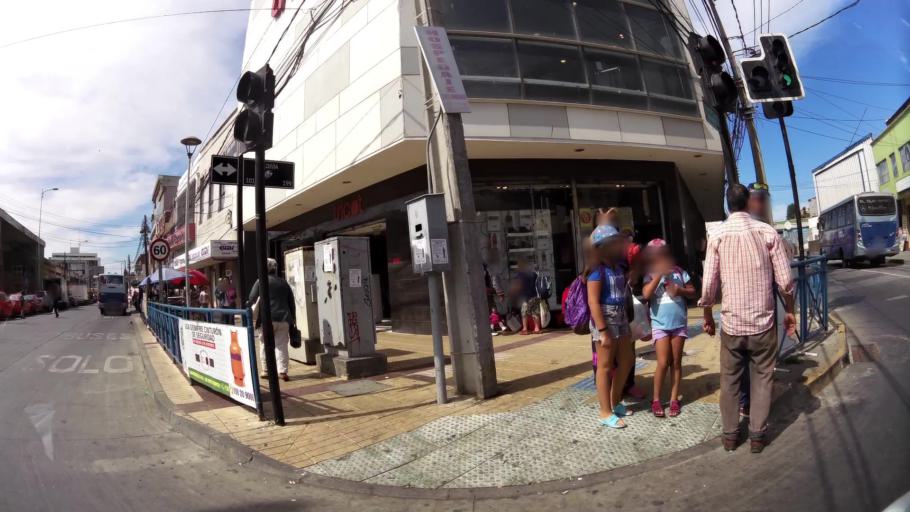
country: CL
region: Biobio
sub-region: Provincia de Concepcion
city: Talcahuano
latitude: -36.7121
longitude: -73.1152
